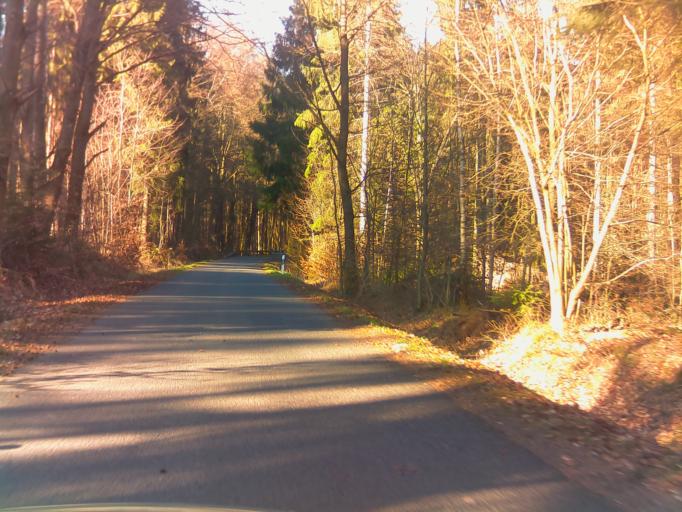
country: DE
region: Bavaria
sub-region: Regierungsbezirk Unterfranken
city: Willmars
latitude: 50.4998
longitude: 10.2994
